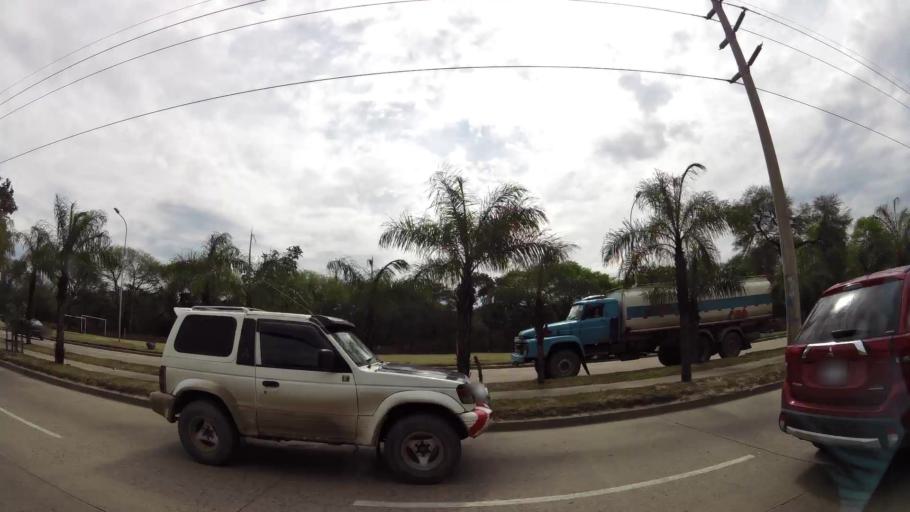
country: BO
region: Santa Cruz
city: Santa Cruz de la Sierra
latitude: -17.7715
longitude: -63.2108
